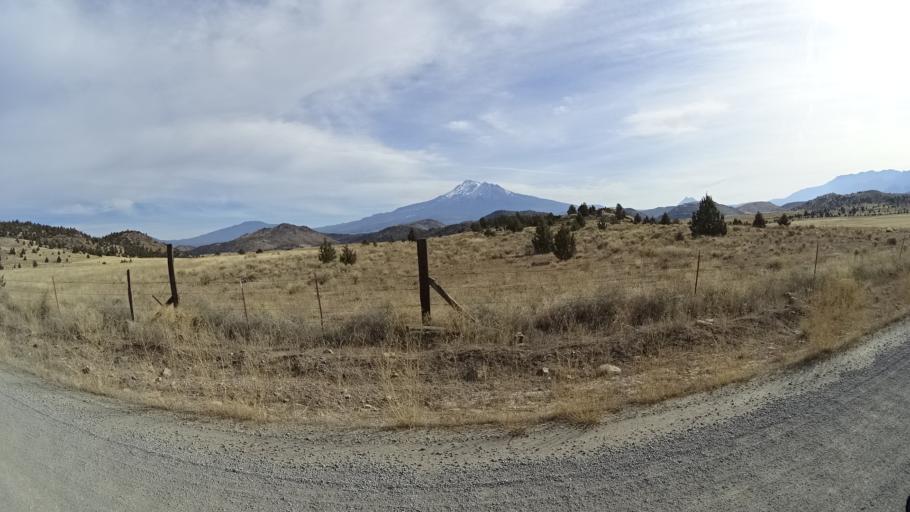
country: US
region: California
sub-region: Siskiyou County
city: Weed
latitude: 41.5619
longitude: -122.4694
